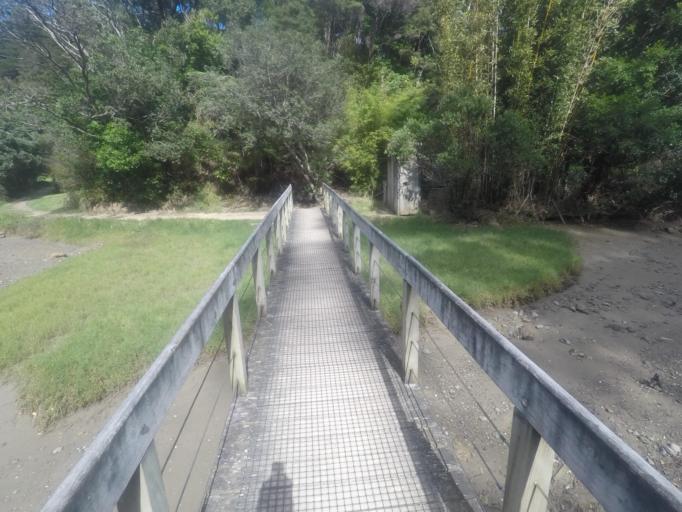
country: NZ
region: Auckland
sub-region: Auckland
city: Warkworth
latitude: -36.2861
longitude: 174.8044
